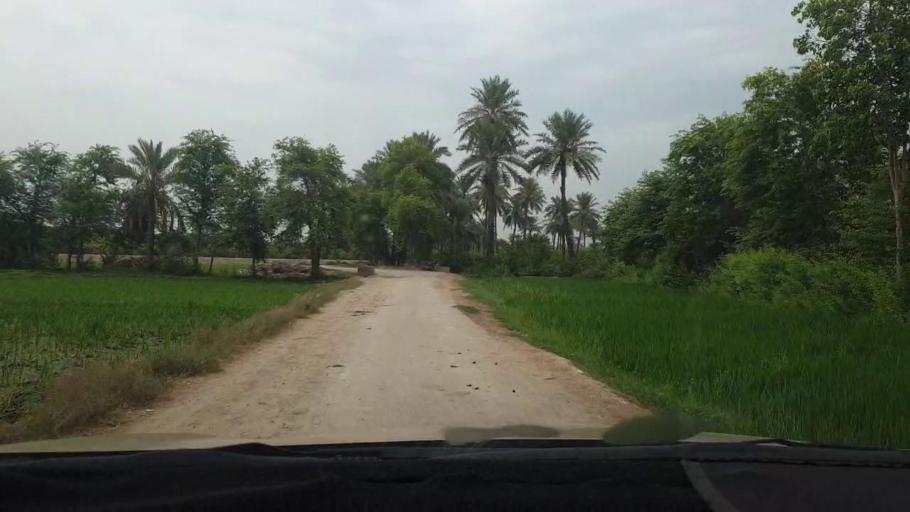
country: PK
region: Sindh
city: Larkana
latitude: 27.5727
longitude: 68.2443
